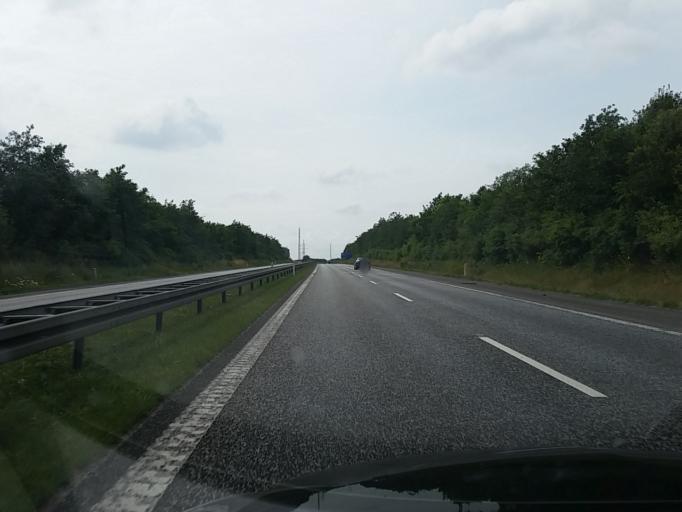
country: DK
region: South Denmark
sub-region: Kolding Kommune
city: Lunderskov
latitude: 55.5082
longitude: 9.3455
